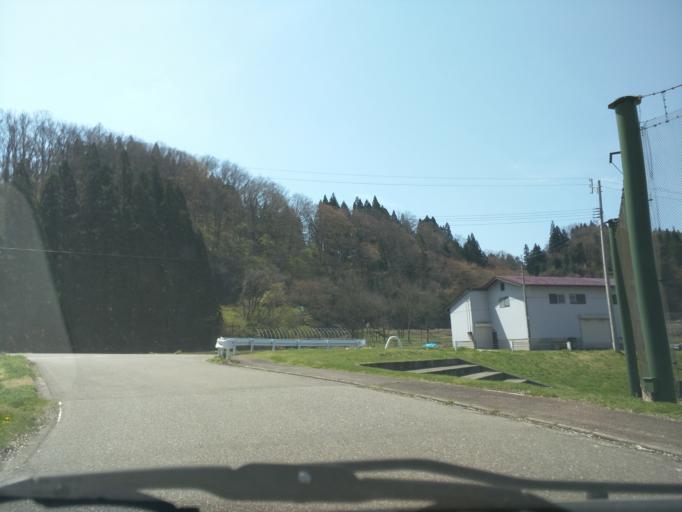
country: JP
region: Fukushima
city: Kitakata
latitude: 37.5220
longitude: 139.7212
